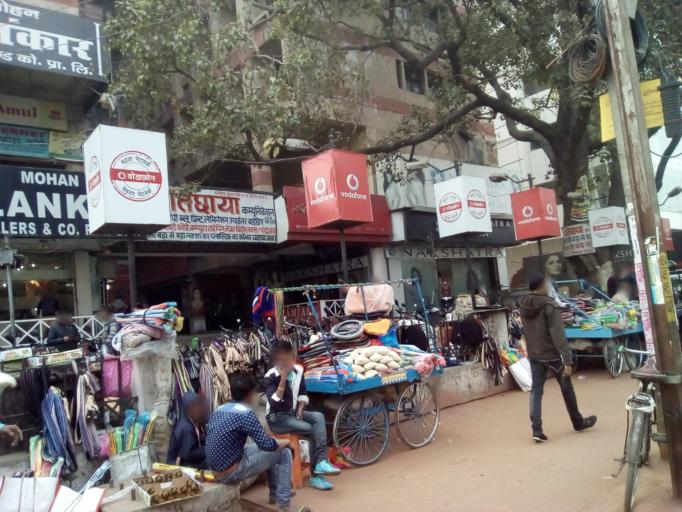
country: IN
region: Bihar
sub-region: Patna
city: Patna
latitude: 25.6100
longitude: 85.1373
